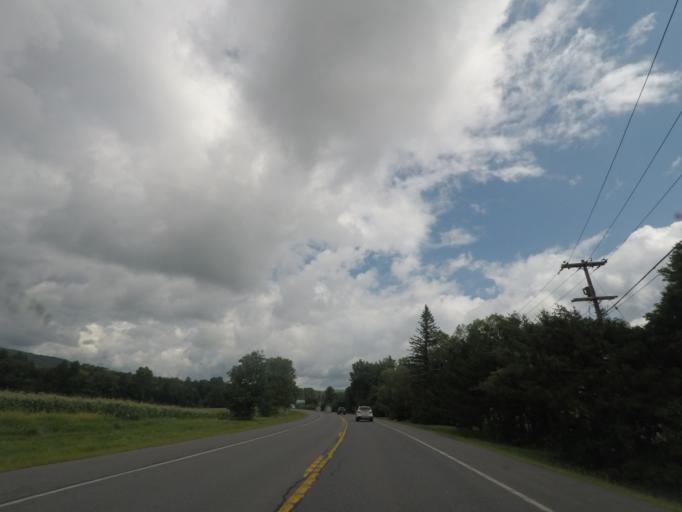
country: US
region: Massachusetts
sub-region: Berkshire County
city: Lanesborough
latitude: 42.5648
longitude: -73.3691
